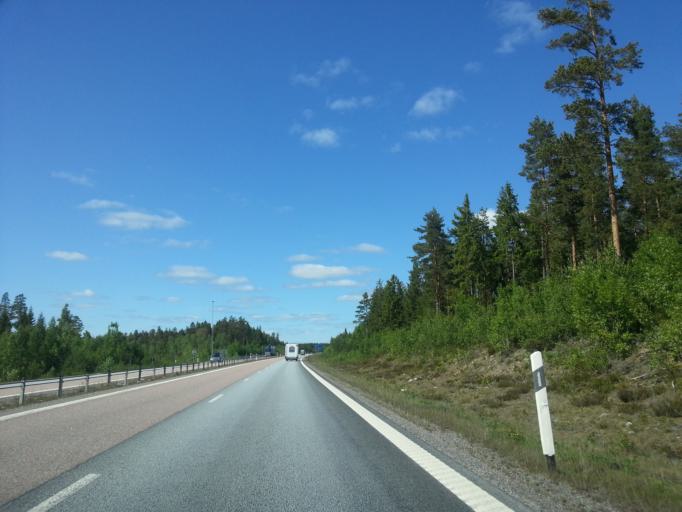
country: SE
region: Gaevleborg
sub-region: Soderhamns Kommun
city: Soderhamn
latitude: 61.4151
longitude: 16.9892
